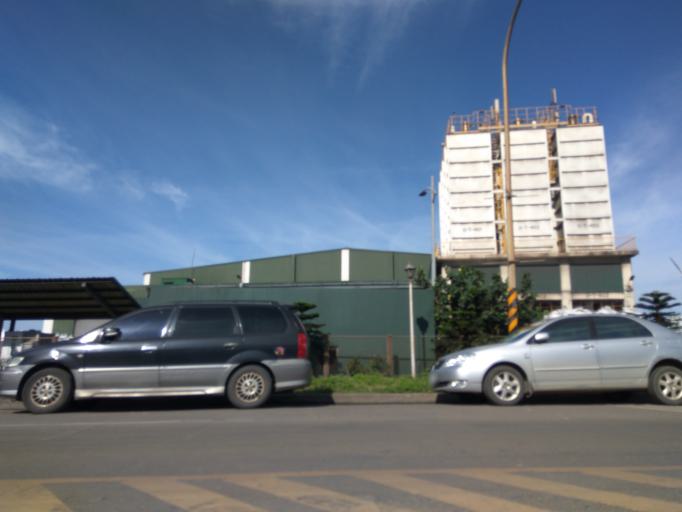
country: TW
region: Taiwan
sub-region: Hsinchu
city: Zhubei
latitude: 25.0346
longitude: 121.0566
